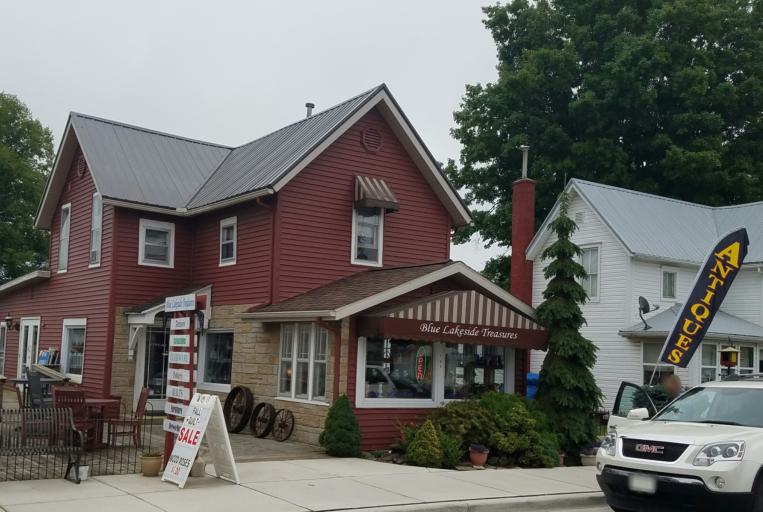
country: US
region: Indiana
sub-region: Elkhart County
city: Middlebury
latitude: 41.6773
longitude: -85.5779
